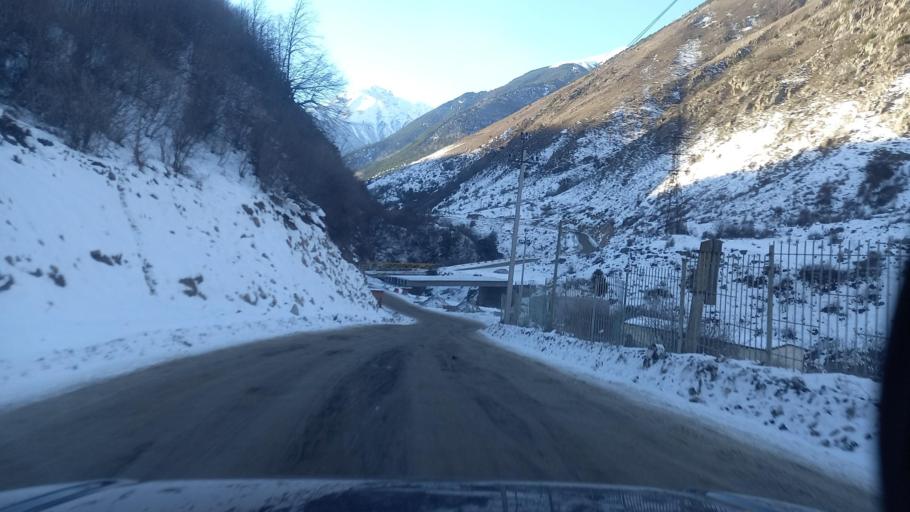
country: RU
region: North Ossetia
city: Chikola
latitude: 42.9805
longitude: 43.7736
